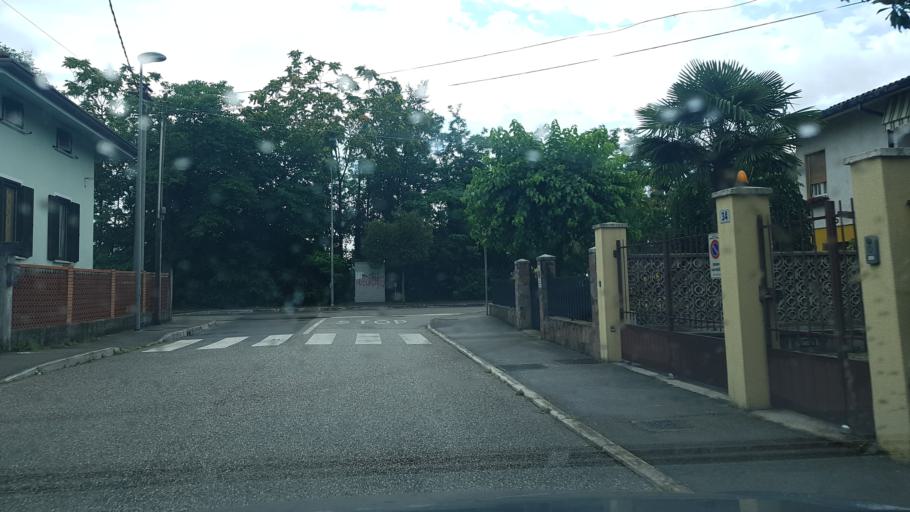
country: IT
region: Friuli Venezia Giulia
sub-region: Provincia di Gorizia
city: Sagrado
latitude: 45.8842
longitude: 13.4863
